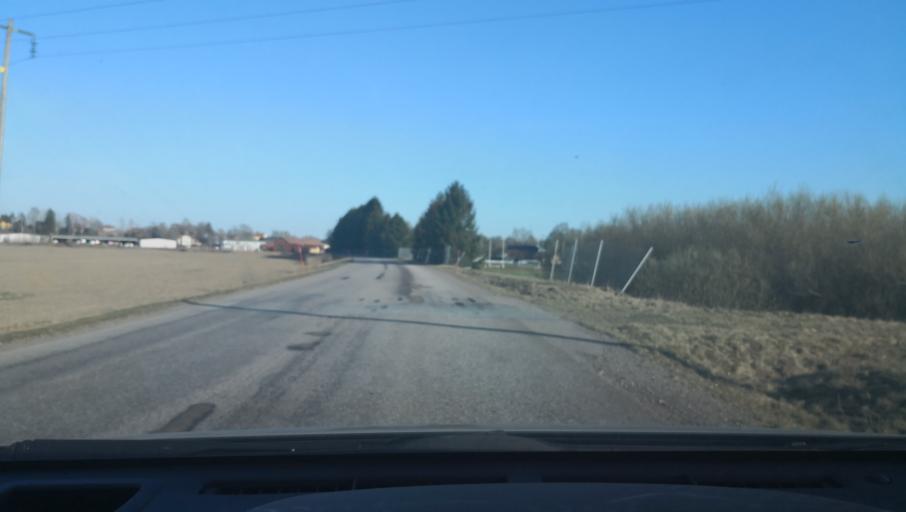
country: SE
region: Uppsala
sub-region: Heby Kommun
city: Heby
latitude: 59.9468
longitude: 16.8463
